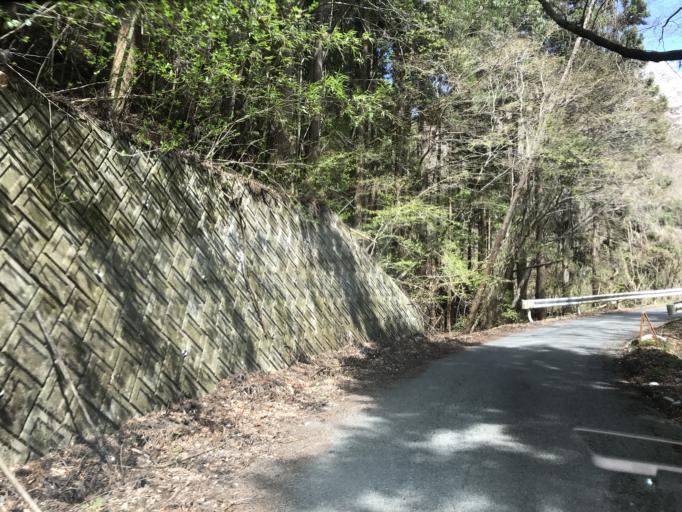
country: JP
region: Iwate
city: Ichinoseki
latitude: 38.7972
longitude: 141.2572
